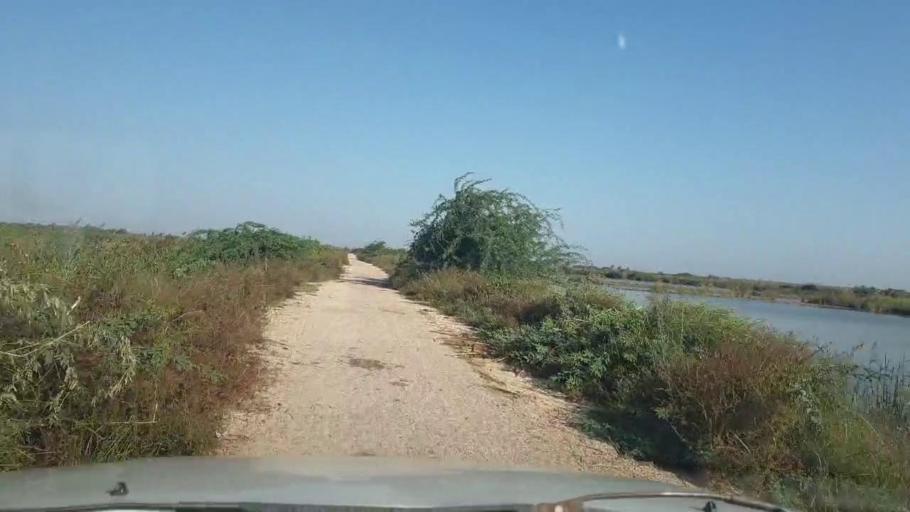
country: PK
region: Sindh
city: Chuhar Jamali
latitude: 24.5508
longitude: 67.9095
